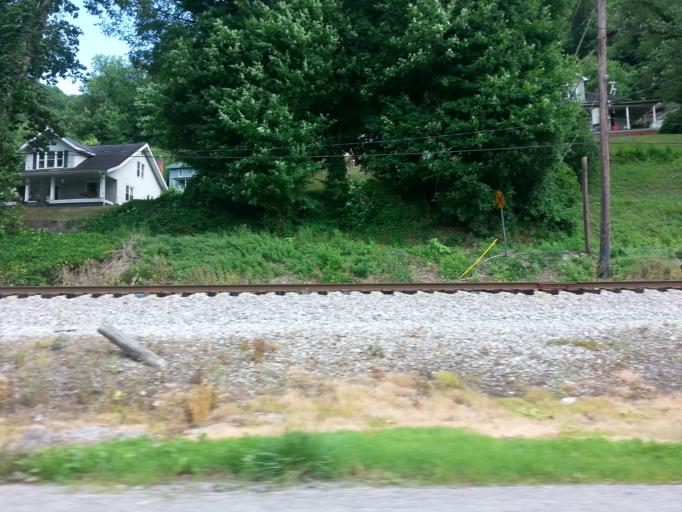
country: US
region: Kentucky
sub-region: Harlan County
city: Harlan
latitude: 36.8452
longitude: -83.3164
